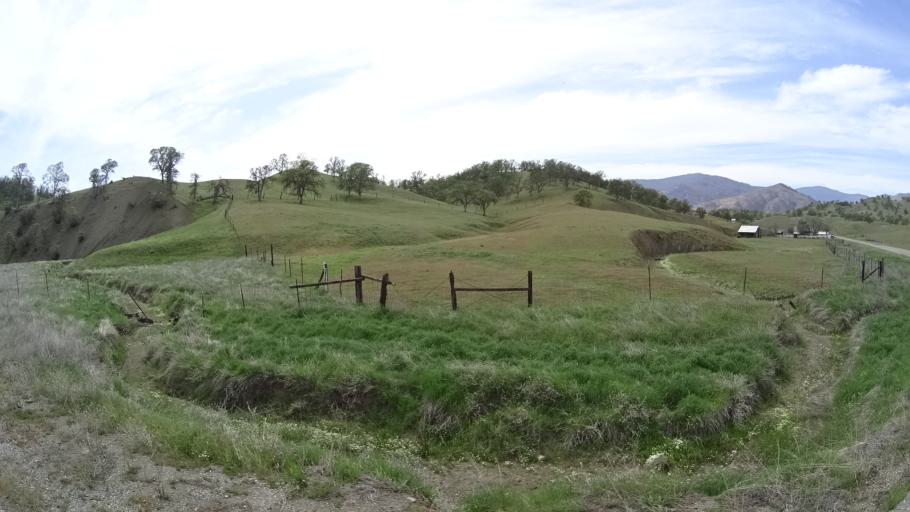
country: US
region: California
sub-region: Glenn County
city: Willows
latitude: 39.6136
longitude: -122.5683
